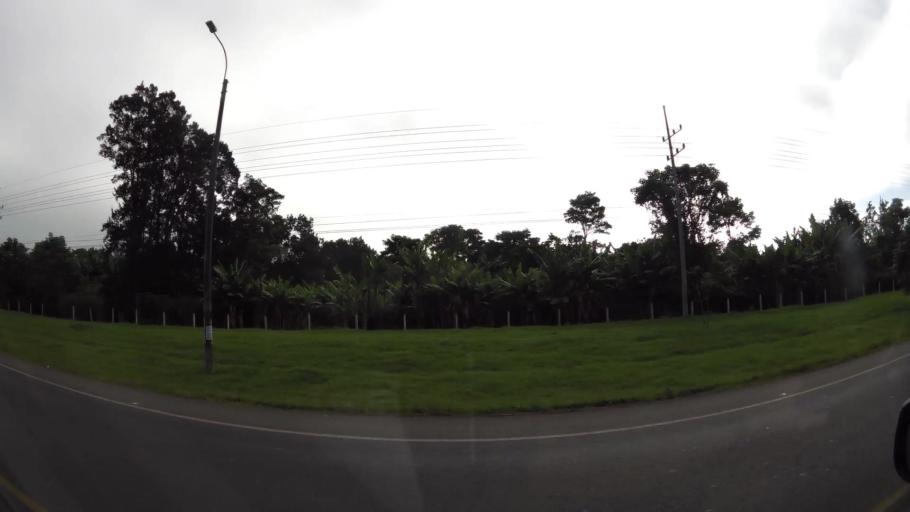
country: CR
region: Cartago
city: Cartago
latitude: 9.8603
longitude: -83.9467
